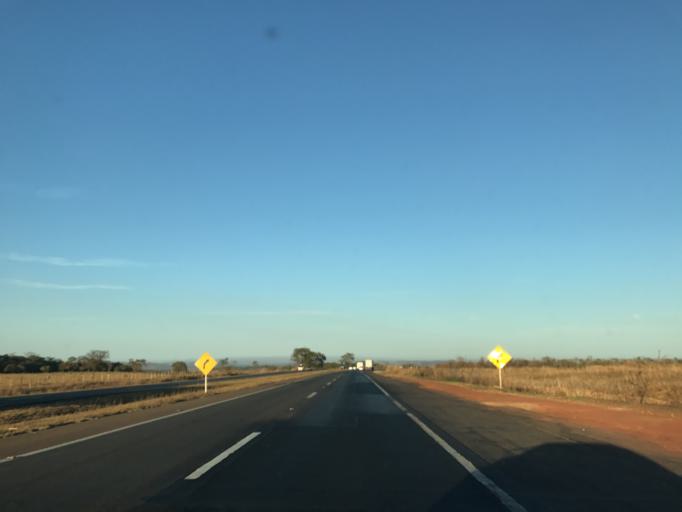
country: BR
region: Goias
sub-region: Anapolis
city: Anapolis
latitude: -16.4076
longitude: -48.9870
